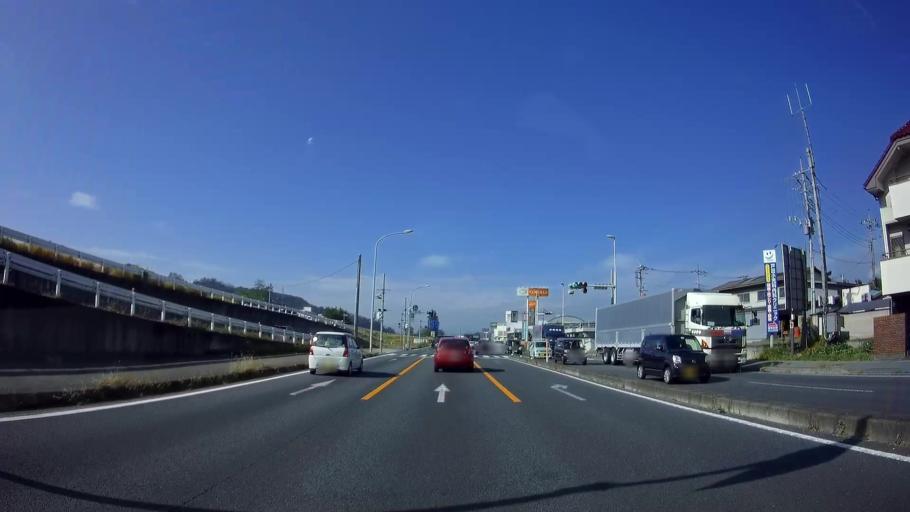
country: JP
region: Gunma
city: Annaka
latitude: 36.3336
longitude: 138.9526
